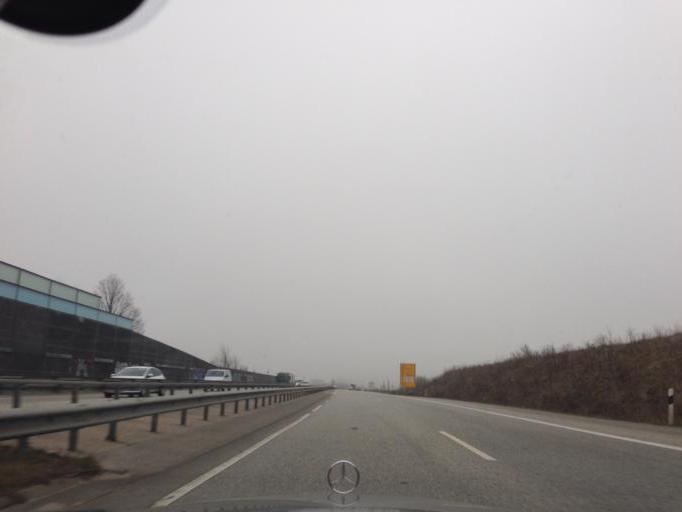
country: DE
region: Schleswig-Holstein
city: Kiel
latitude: 54.2795
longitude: 10.1377
